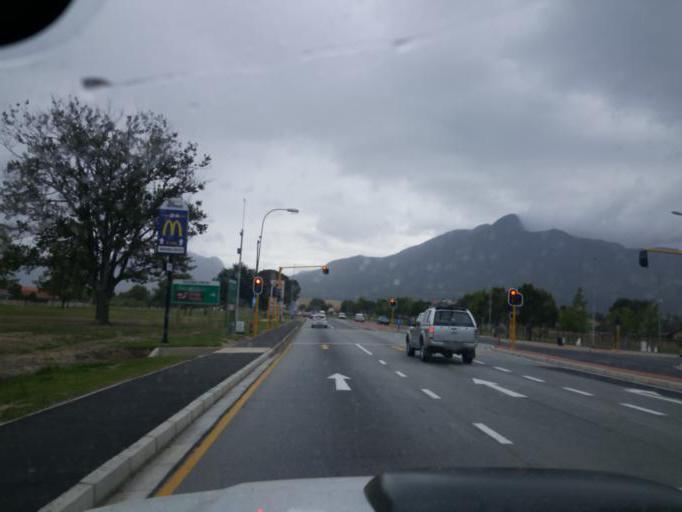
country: ZA
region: Western Cape
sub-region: Eden District Municipality
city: George
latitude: -33.9692
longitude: 22.4876
